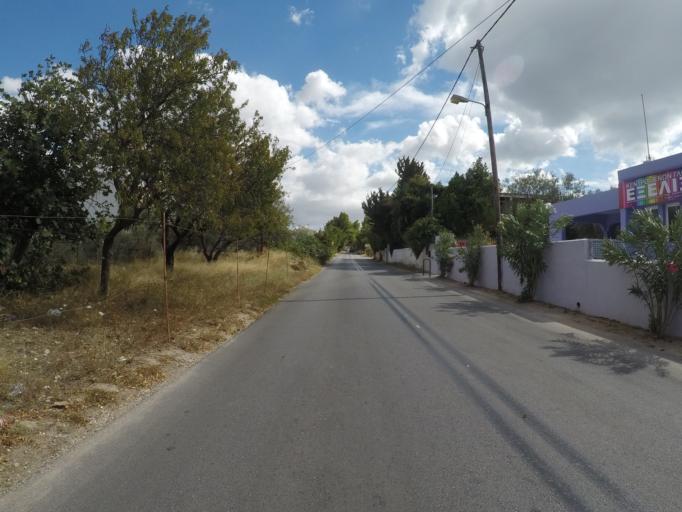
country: GR
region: Attica
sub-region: Nomarchia Anatolikis Attikis
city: Agia Marina
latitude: 37.8254
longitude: 23.8603
